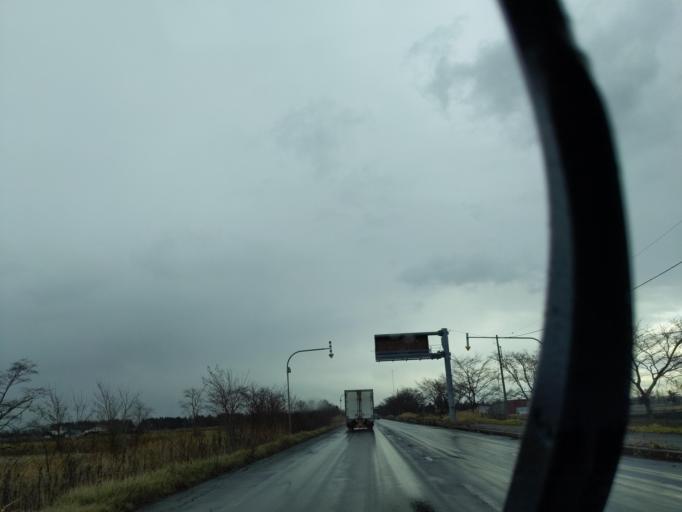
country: JP
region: Hokkaido
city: Ebetsu
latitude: 43.1106
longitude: 141.5910
